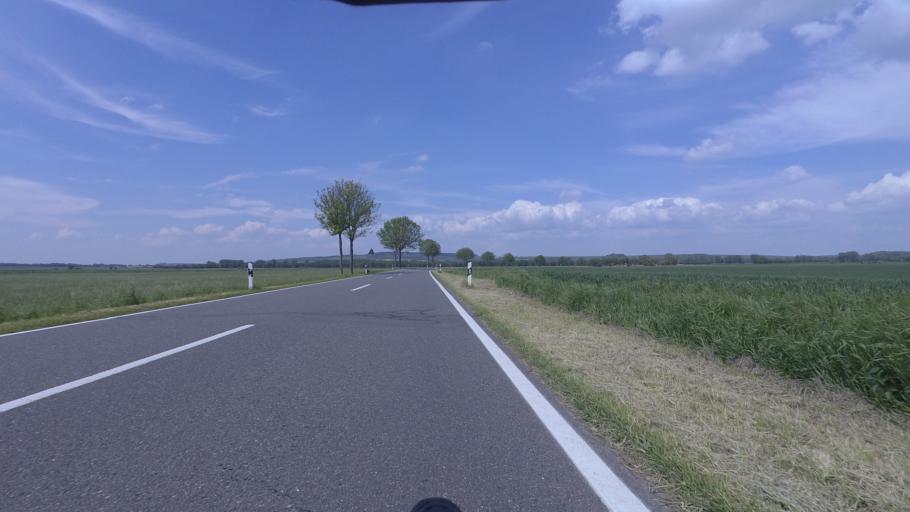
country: DE
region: Lower Saxony
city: Jerxheim
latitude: 52.0512
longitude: 10.8839
